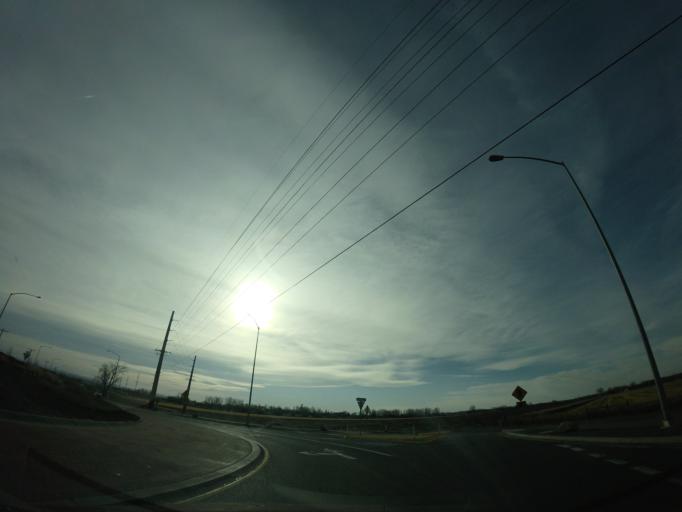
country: US
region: Montana
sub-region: Yellowstone County
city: Billings
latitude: 45.7766
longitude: -108.6178
